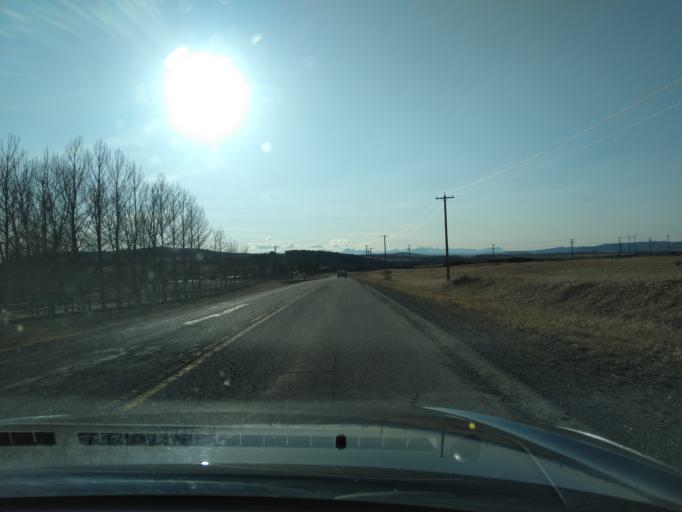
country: CA
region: Alberta
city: Cochrane
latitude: 51.1682
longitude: -114.4864
